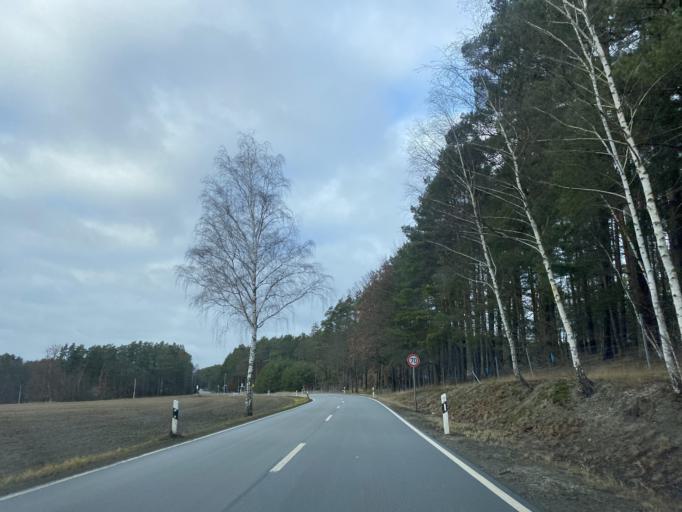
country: PL
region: Lubusz
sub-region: Powiat zarski
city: Leknica
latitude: 51.5122
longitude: 14.7759
